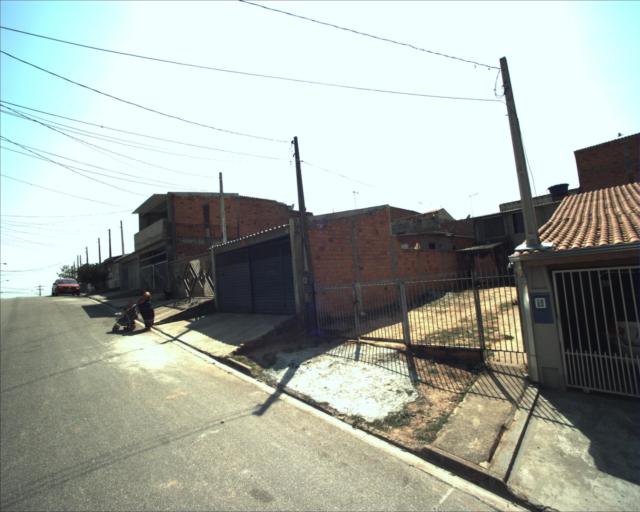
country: BR
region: Sao Paulo
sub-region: Sorocaba
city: Sorocaba
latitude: -23.4351
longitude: -47.4882
